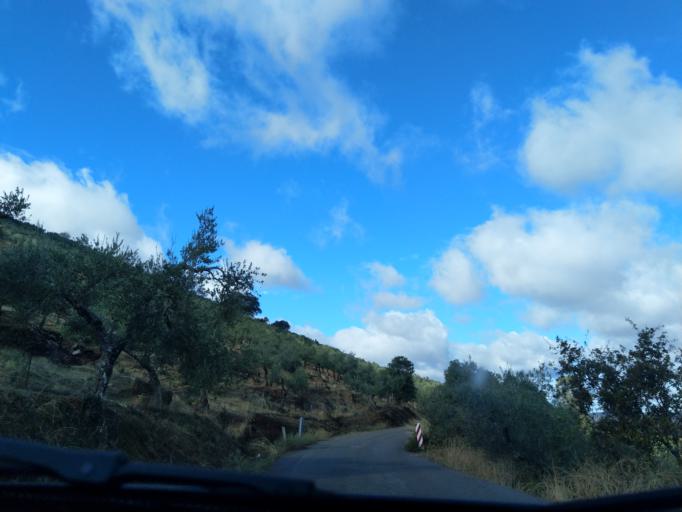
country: ES
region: Extremadura
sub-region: Provincia de Badajoz
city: Reina
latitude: 38.1269
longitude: -5.9203
